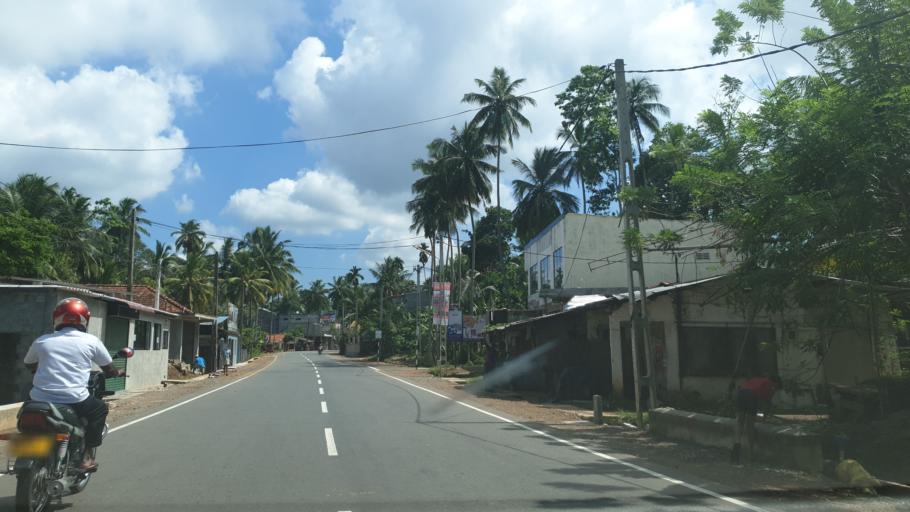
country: LK
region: Western
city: Panadura
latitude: 6.6700
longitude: 79.9401
